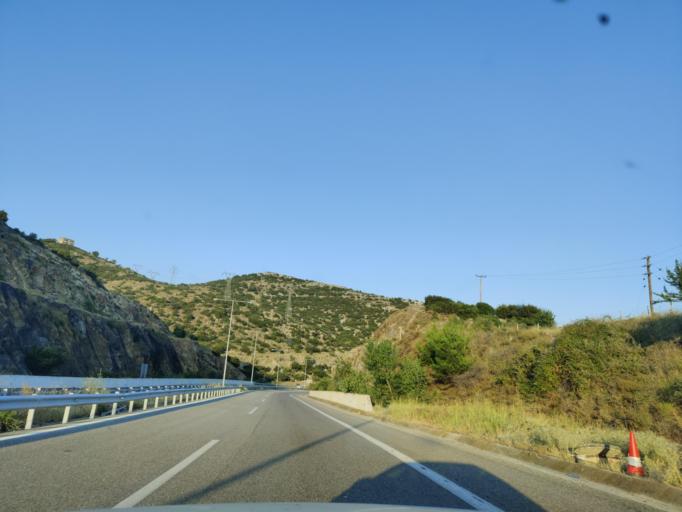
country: GR
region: East Macedonia and Thrace
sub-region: Nomos Kavalas
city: Kavala
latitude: 40.9602
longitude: 24.4392
